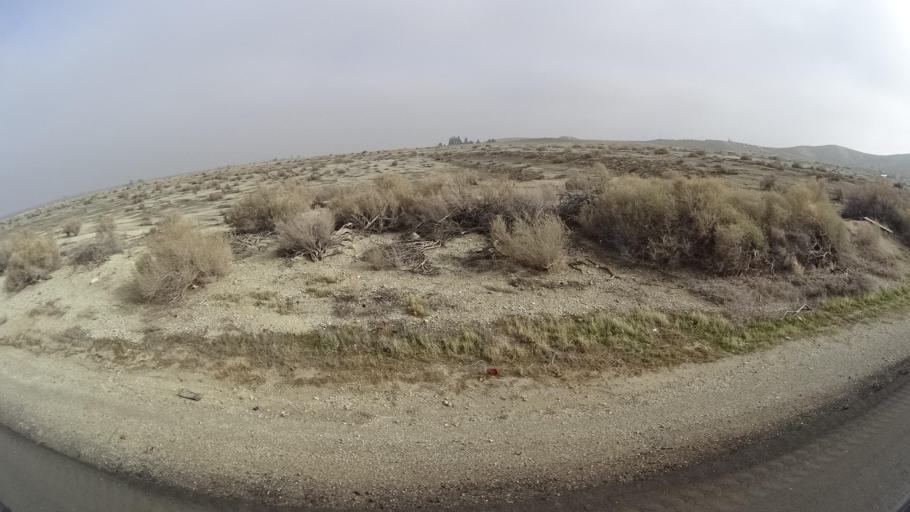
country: US
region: California
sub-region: Kern County
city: Maricopa
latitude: 35.0407
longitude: -119.3670
